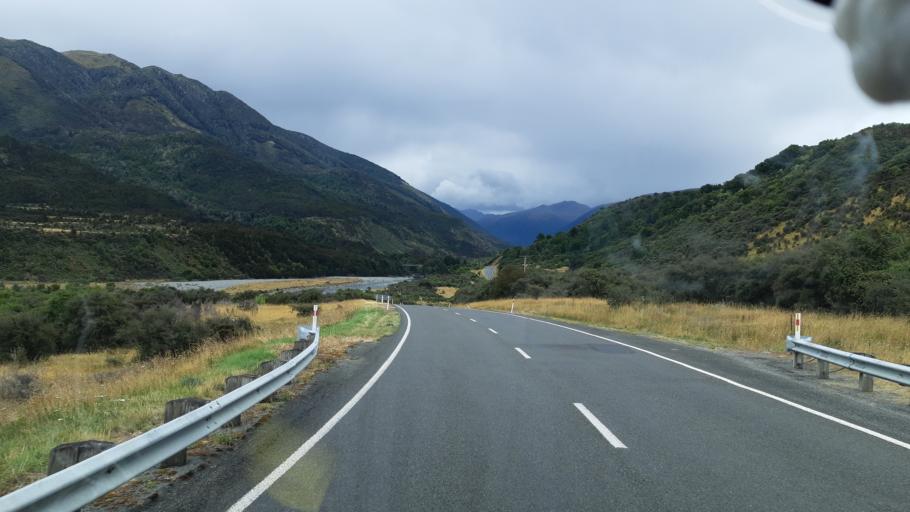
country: NZ
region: Canterbury
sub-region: Hurunui District
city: Amberley
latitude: -42.5750
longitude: 172.3740
